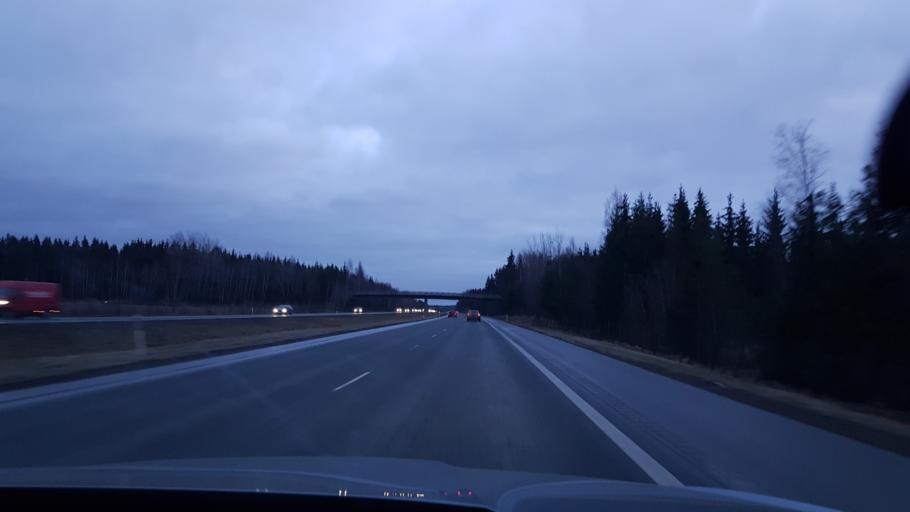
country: FI
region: Haeme
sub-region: Haemeenlinna
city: Tervakoski
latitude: 60.7968
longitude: 24.6885
